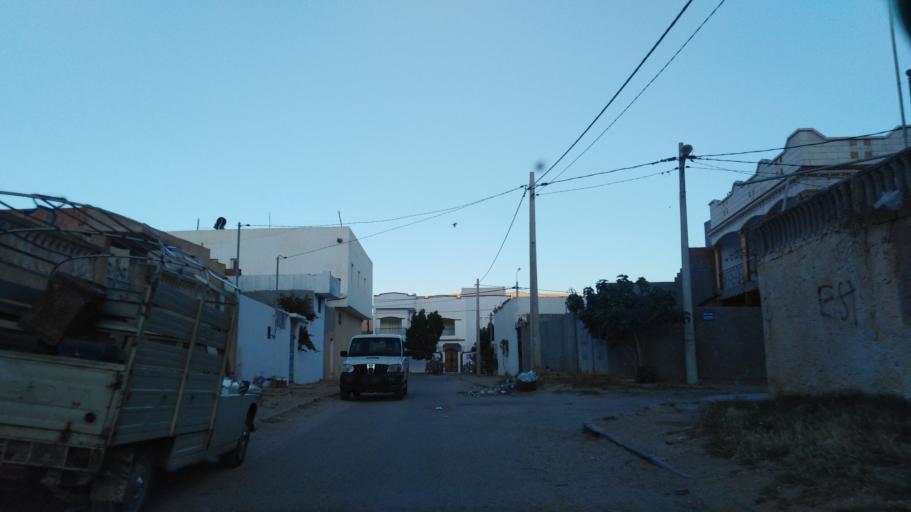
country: TN
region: Tataouine
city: Tataouine
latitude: 32.9414
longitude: 10.4555
